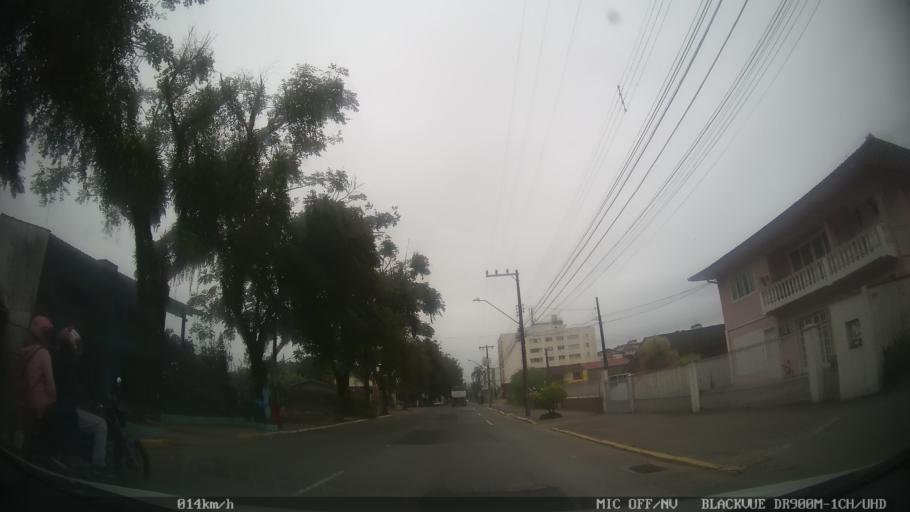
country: BR
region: Santa Catarina
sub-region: Joinville
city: Joinville
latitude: -26.3143
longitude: -48.8359
